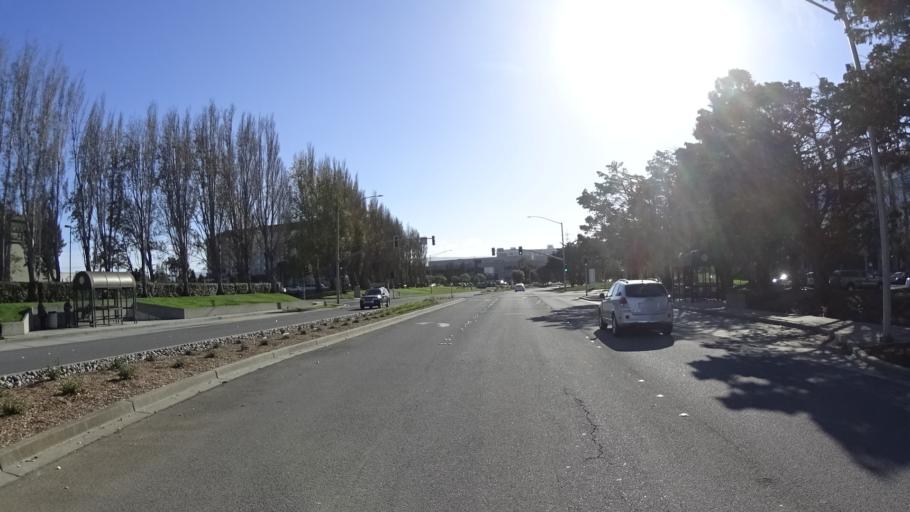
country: US
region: California
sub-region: San Mateo County
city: South San Francisco
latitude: 37.6593
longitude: -122.3971
